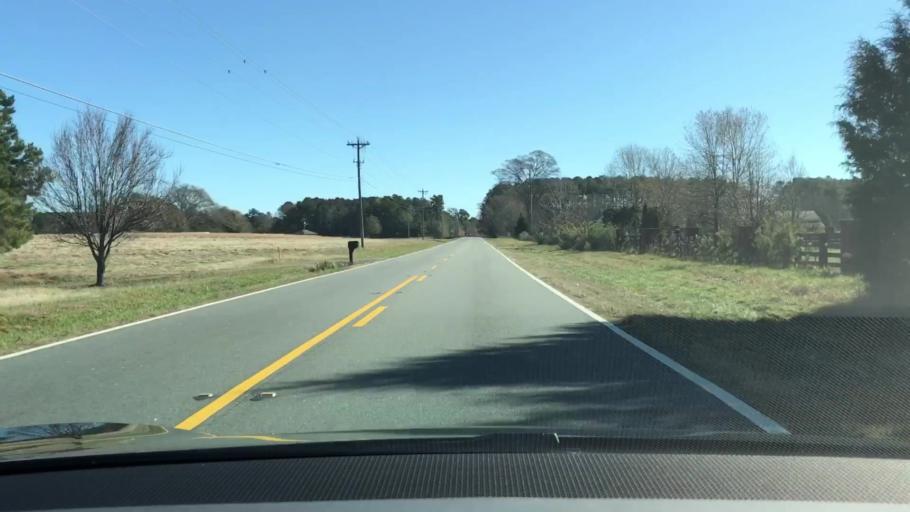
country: US
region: Georgia
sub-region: Walton County
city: Monroe
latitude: 33.8615
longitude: -83.7449
